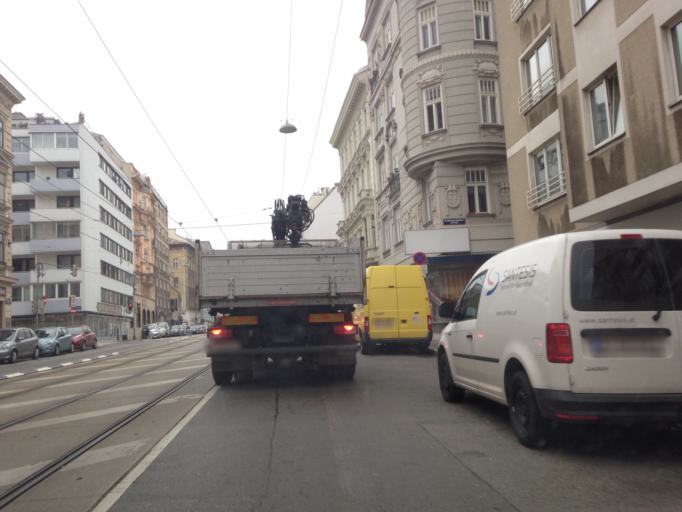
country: AT
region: Vienna
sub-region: Wien Stadt
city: Vienna
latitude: 48.2269
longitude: 16.3552
